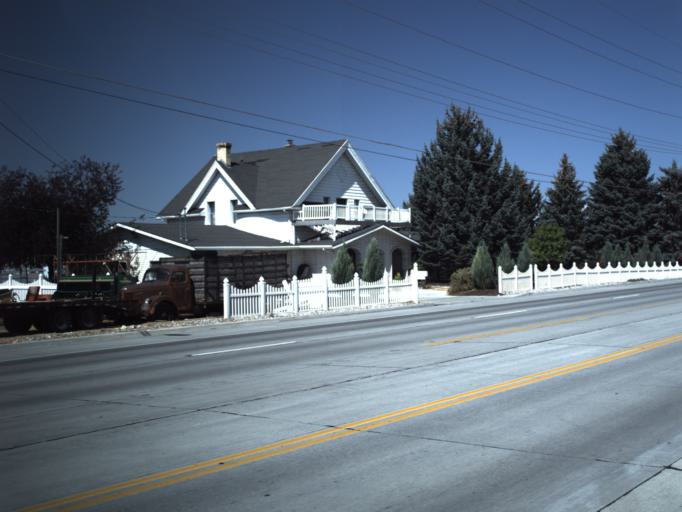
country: US
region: Utah
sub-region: Cache County
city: Logan
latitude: 41.7179
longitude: -111.8599
